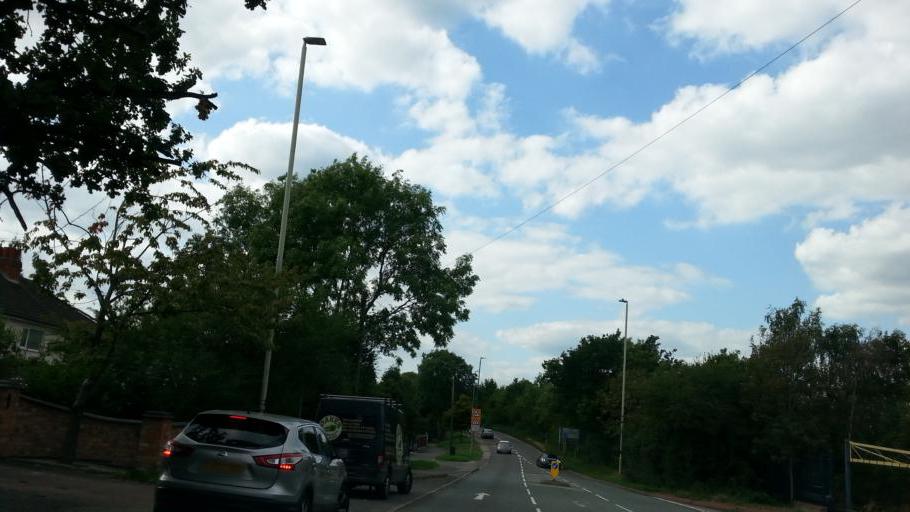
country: GB
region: England
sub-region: Leicestershire
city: Glenfield
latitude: 52.6278
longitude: -1.2029
